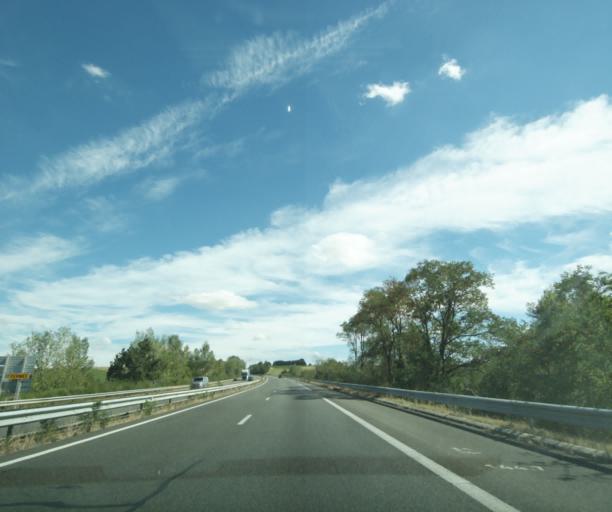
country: FR
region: Midi-Pyrenees
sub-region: Departement du Tarn-et-Garonne
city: Lamagistere
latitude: 44.0719
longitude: 0.8113
